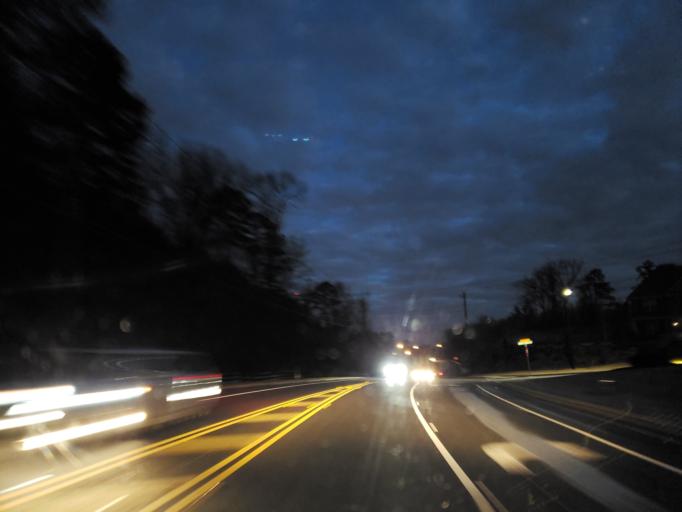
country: US
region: Georgia
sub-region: Cobb County
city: Kennesaw
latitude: 33.9975
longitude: -84.6429
